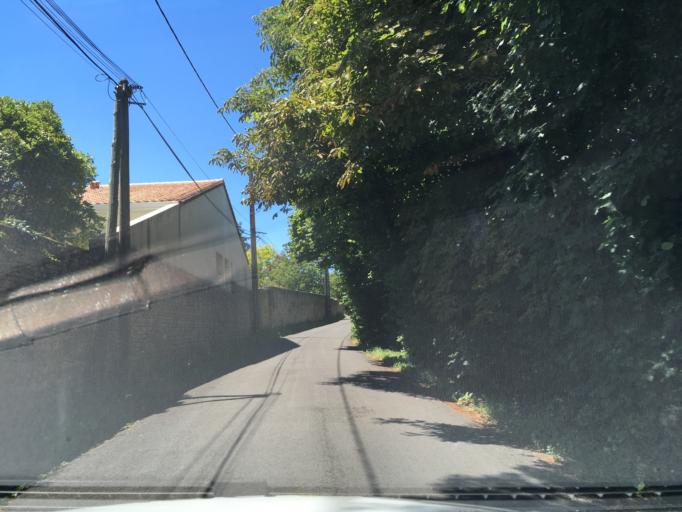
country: FR
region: Poitou-Charentes
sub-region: Departement des Deux-Sevres
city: Niort
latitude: 46.3315
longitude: -0.4414
